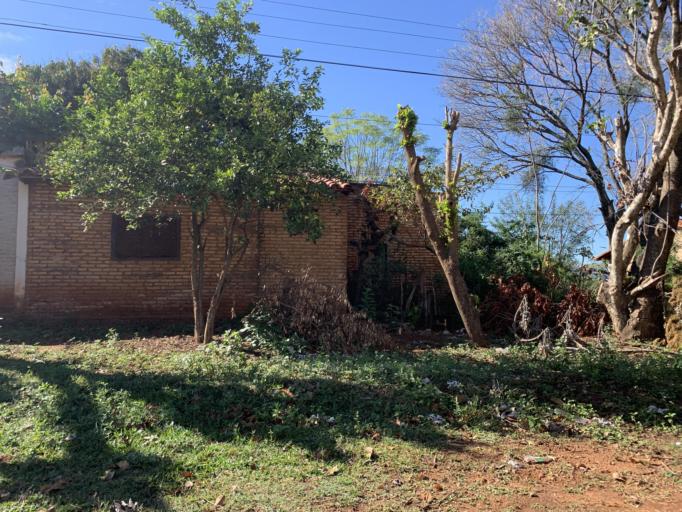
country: PY
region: Misiones
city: San Juan Bautista
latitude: -26.6737
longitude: -57.1396
